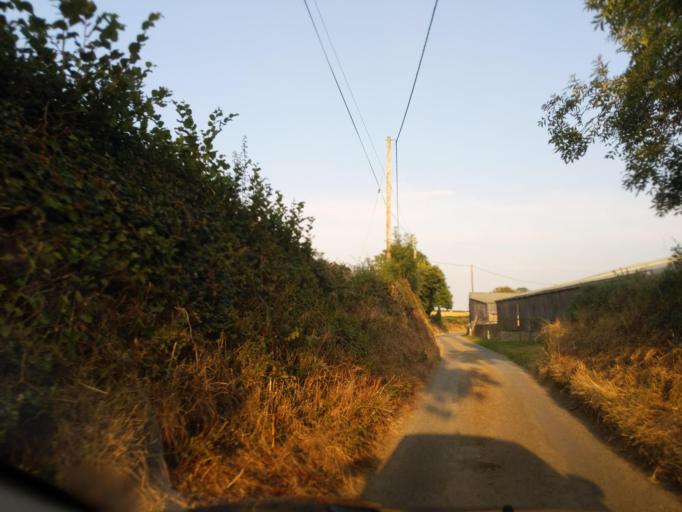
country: GB
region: England
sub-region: Cornwall
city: Fowey
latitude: 50.3685
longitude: -4.5927
